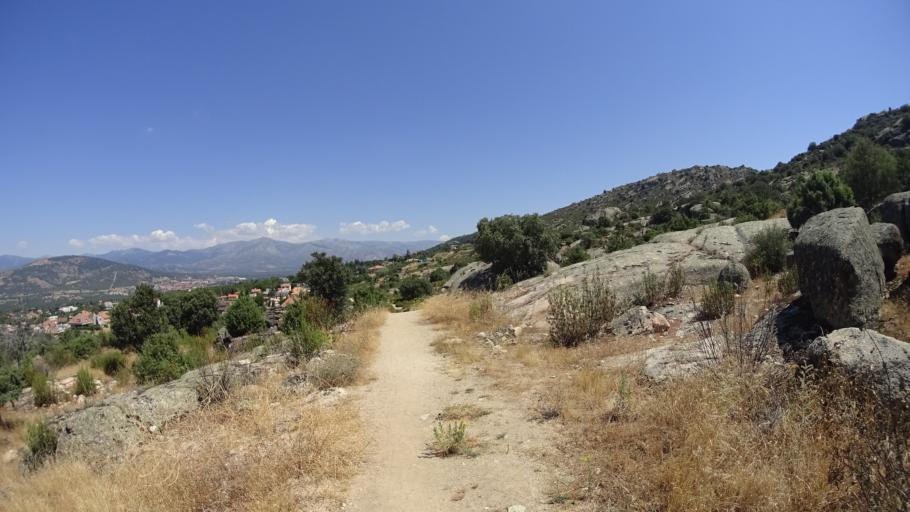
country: ES
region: Madrid
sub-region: Provincia de Madrid
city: Moralzarzal
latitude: 40.6432
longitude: -3.9633
